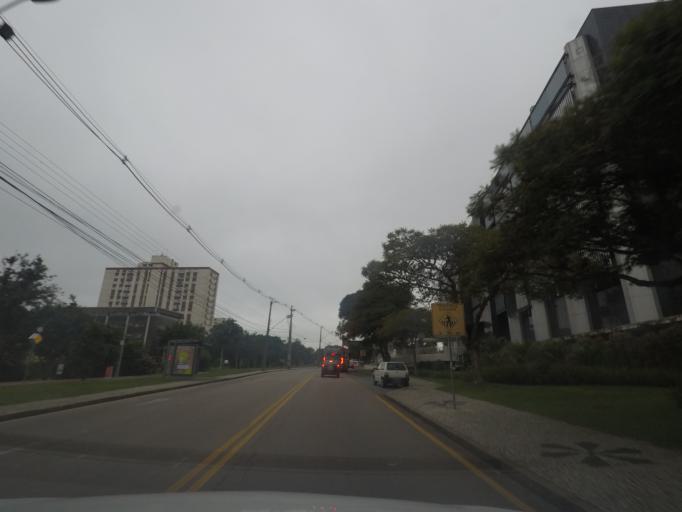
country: BR
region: Parana
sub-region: Curitiba
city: Curitiba
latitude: -25.4156
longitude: -49.2701
